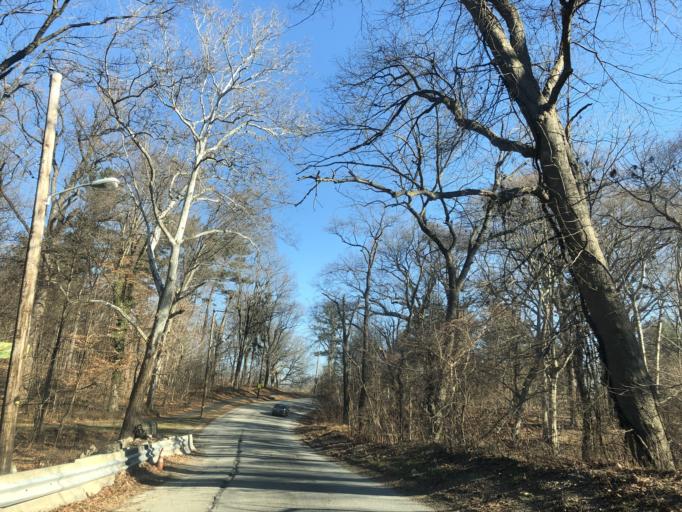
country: US
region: Pennsylvania
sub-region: Montgomery County
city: Bala-Cynwyd
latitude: 39.9962
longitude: -75.2018
